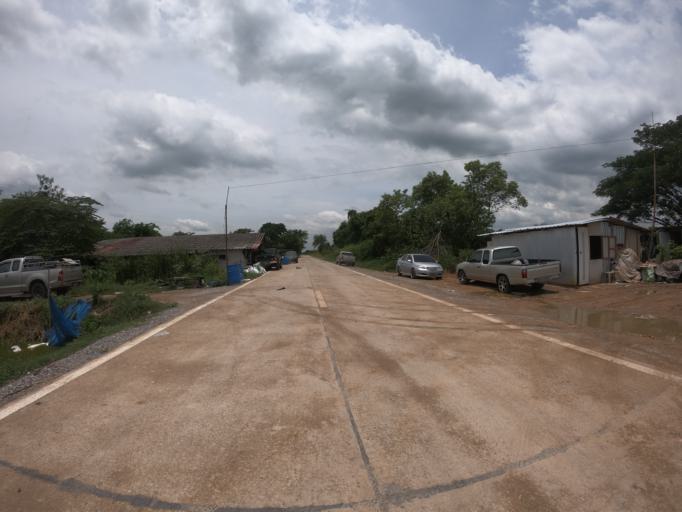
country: TH
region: Pathum Thani
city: Ban Lam Luk Ka
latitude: 13.9815
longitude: 100.8532
